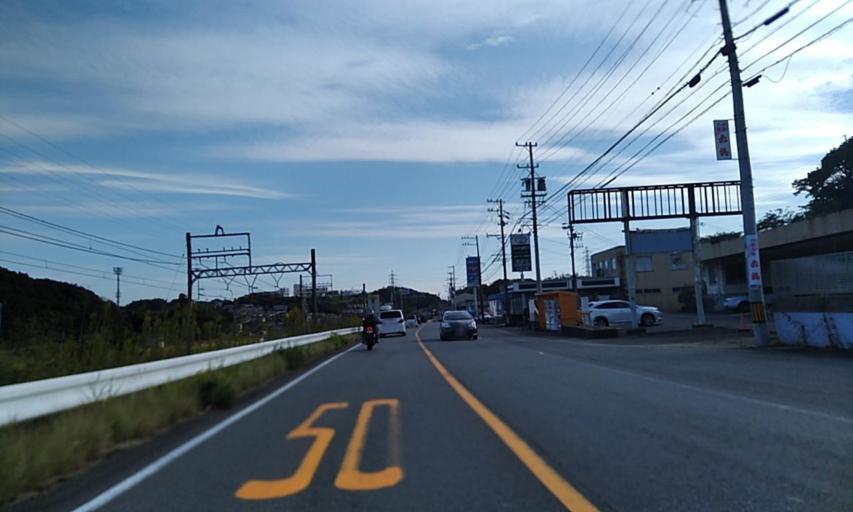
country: JP
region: Mie
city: Toba
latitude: 34.3423
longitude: 136.8164
